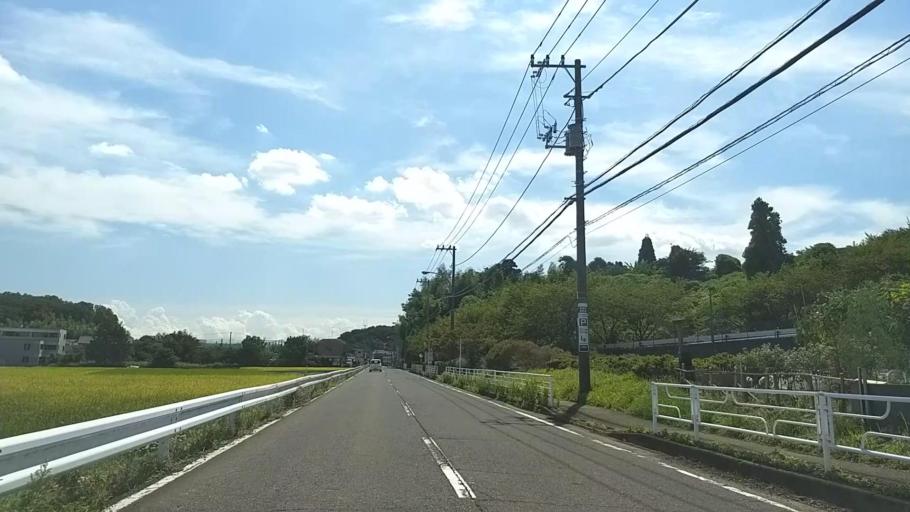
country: JP
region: Tokyo
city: Chofugaoka
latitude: 35.5568
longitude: 139.5654
